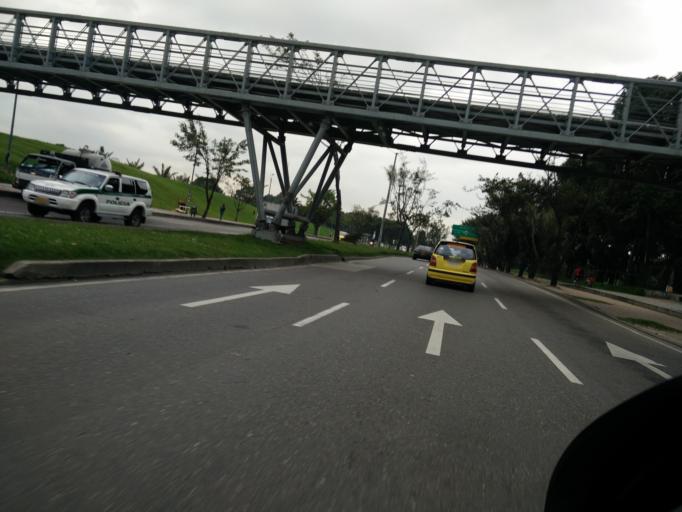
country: CO
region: Bogota D.C.
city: Bogota
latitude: 4.6572
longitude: -74.0870
